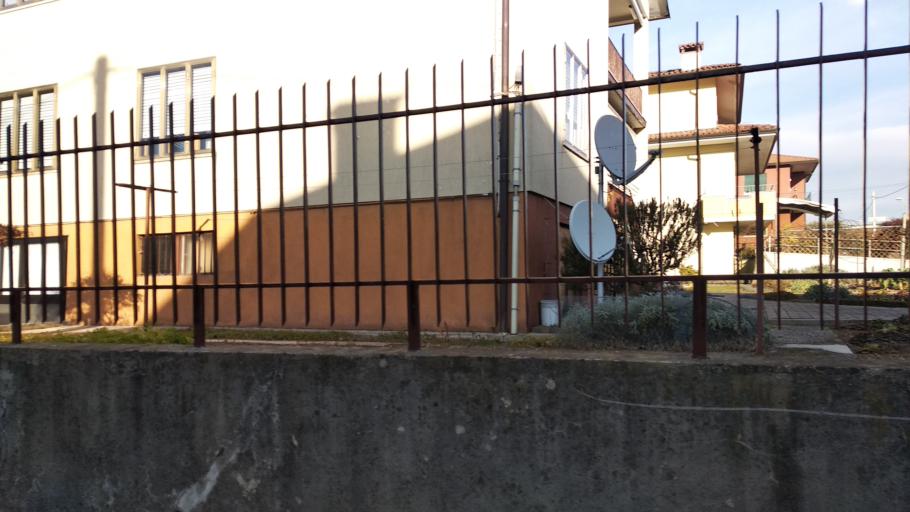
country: IT
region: Veneto
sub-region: Provincia di Vicenza
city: Schio
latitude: 45.6936
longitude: 11.3677
